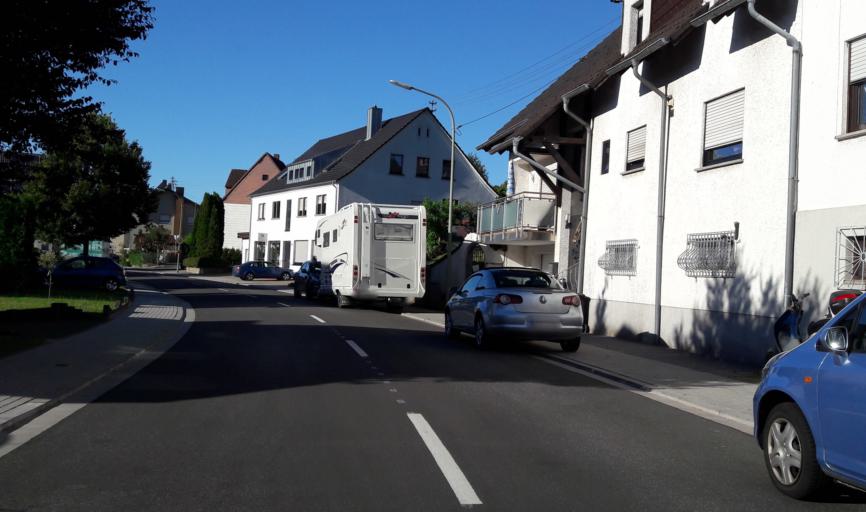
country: DE
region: Rheinland-Pfalz
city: Breitenbach
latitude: 49.4166
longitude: 7.2636
